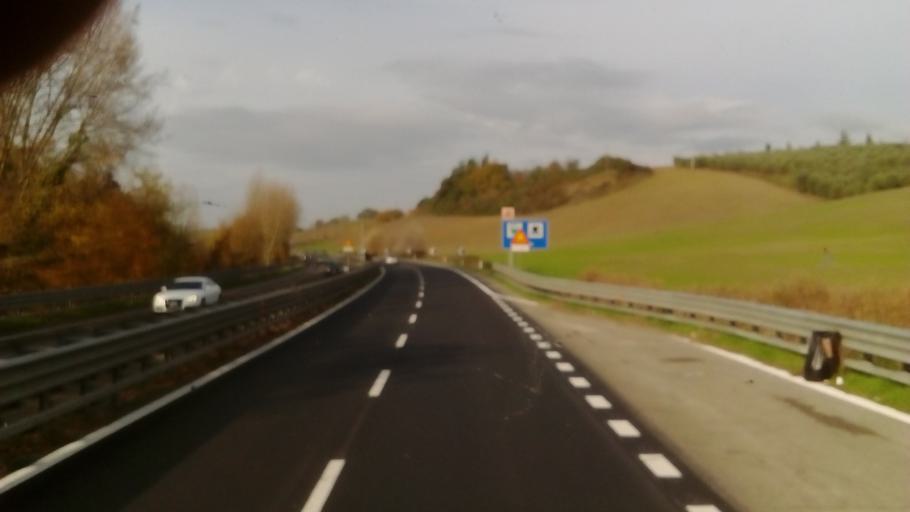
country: IT
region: Tuscany
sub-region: Provincia di Siena
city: Castelnuovo Berardenga
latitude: 43.3193
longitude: 11.4942
